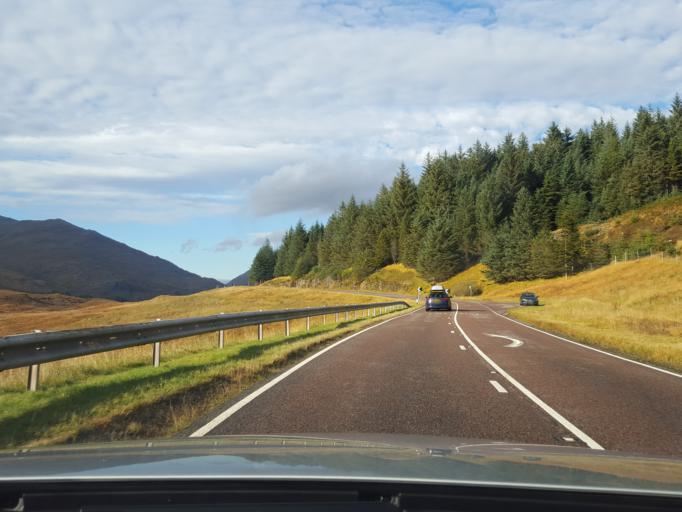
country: GB
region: Scotland
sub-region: Highland
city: Fort William
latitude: 57.1520
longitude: -5.2345
